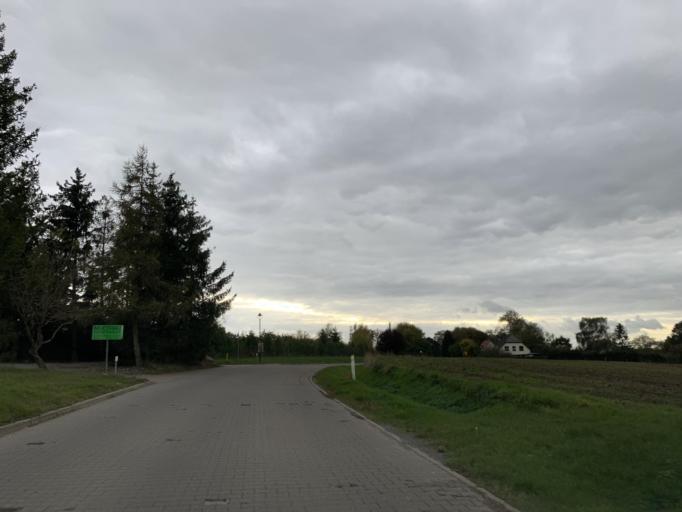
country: DE
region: Mecklenburg-Vorpommern
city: Burg Stargard
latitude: 53.4600
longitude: 13.2912
